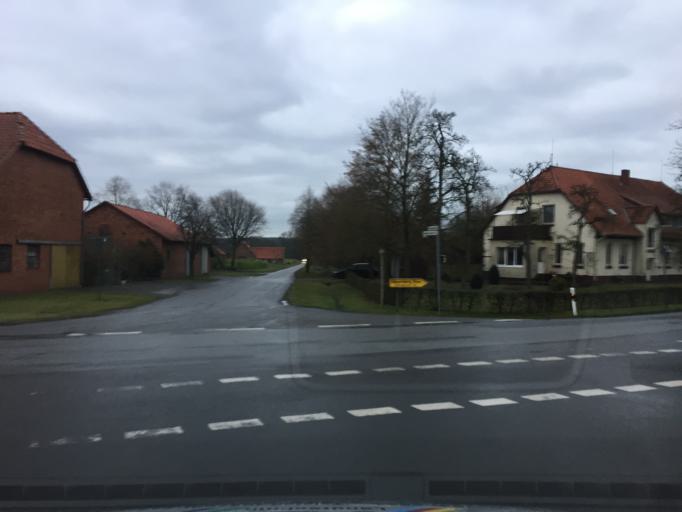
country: DE
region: Lower Saxony
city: Pennigsehl
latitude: 52.6338
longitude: 9.0078
